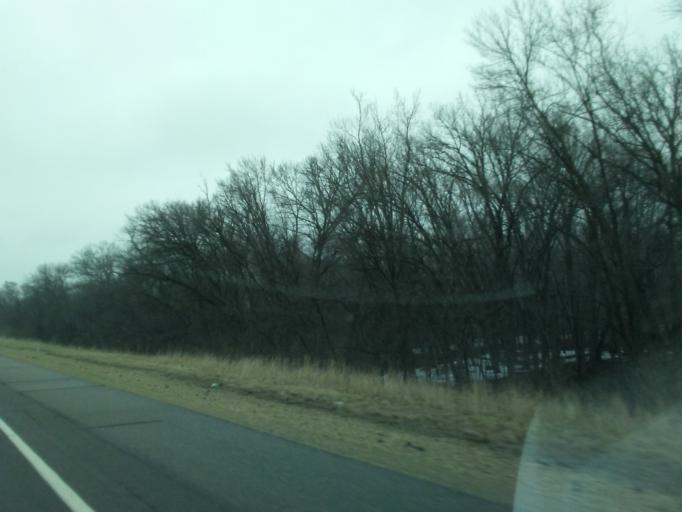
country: US
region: Wisconsin
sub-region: Sauk County
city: Spring Green
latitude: 43.1729
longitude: -90.0469
